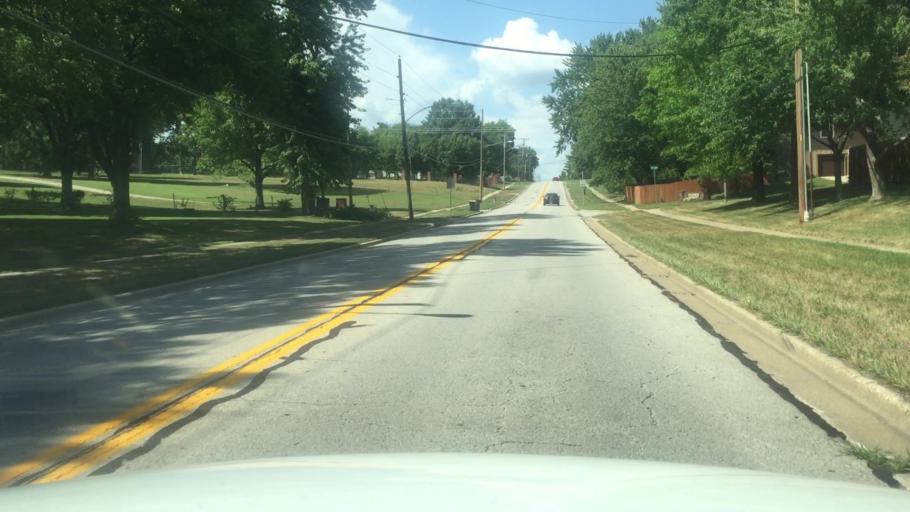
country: US
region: Kansas
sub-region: Johnson County
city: Shawnee
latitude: 39.0018
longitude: -94.7424
